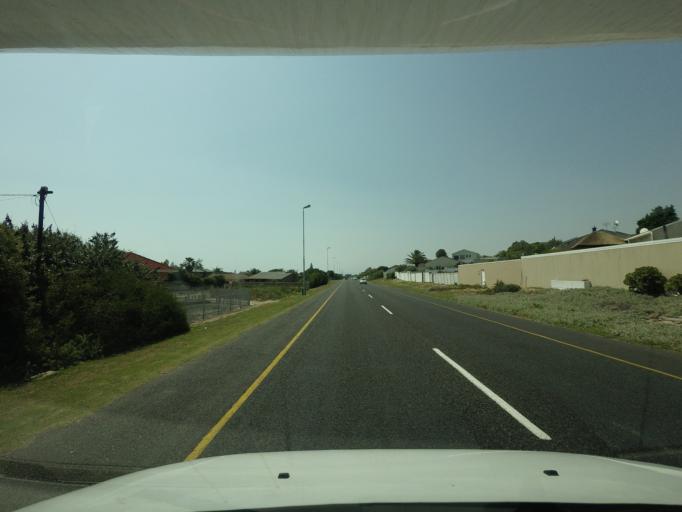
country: ZA
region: Western Cape
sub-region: City of Cape Town
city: Sunset Beach
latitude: -33.7211
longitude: 18.4468
